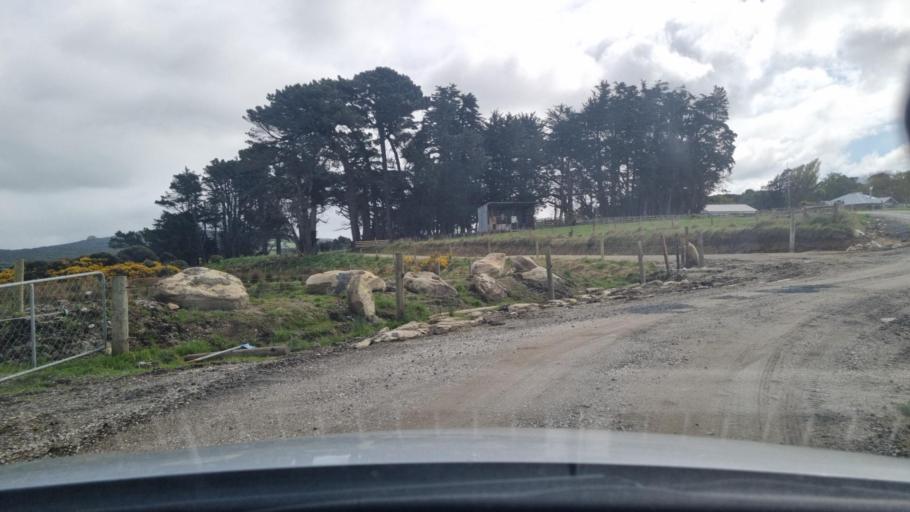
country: NZ
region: Southland
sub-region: Invercargill City
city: Bluff
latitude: -46.5258
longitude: 168.2989
